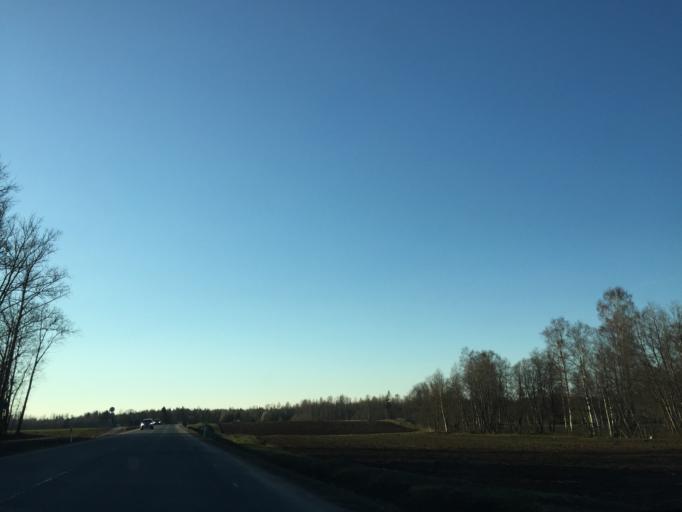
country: EE
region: Ida-Virumaa
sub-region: Johvi vald
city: Johvi
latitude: 59.2061
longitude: 27.5304
